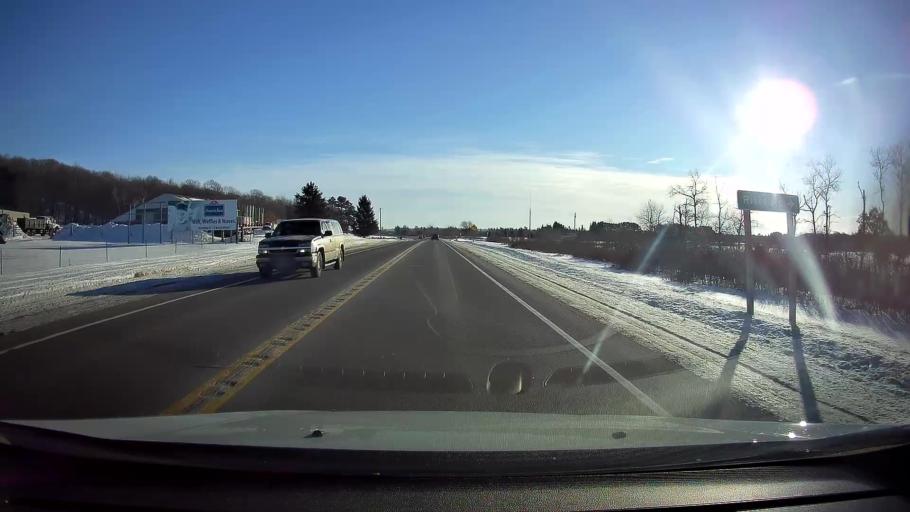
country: US
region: Wisconsin
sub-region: Sawyer County
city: Hayward
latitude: 45.9822
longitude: -91.5645
